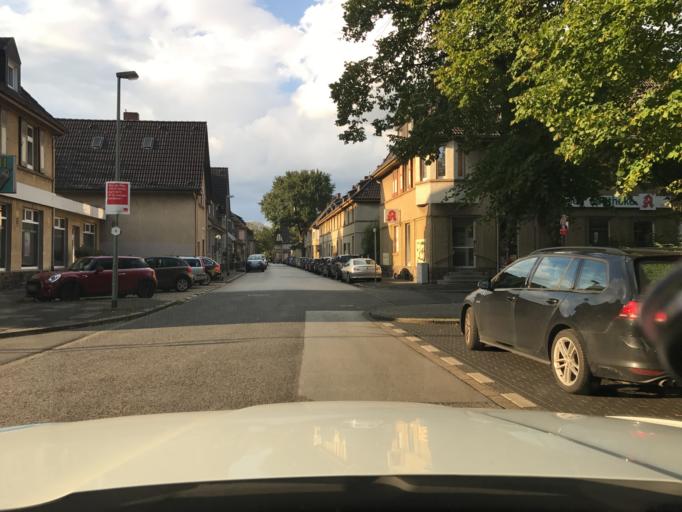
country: DE
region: North Rhine-Westphalia
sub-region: Regierungsbezirk Dusseldorf
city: Hochfeld
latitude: 51.3917
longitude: 6.7965
